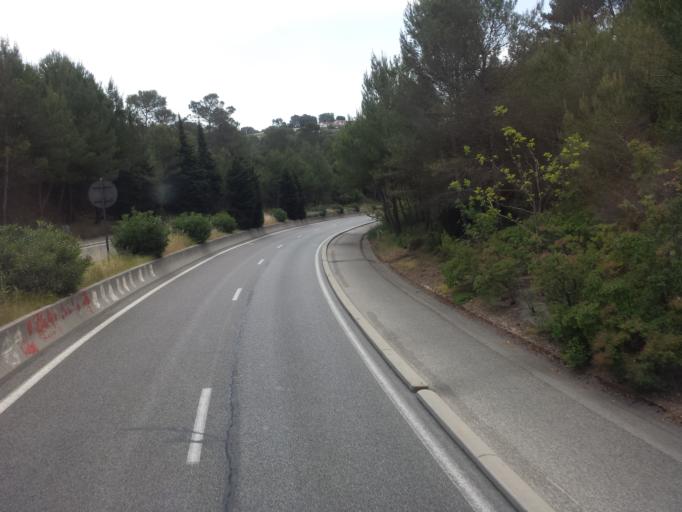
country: FR
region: Provence-Alpes-Cote d'Azur
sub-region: Departement des Alpes-Maritimes
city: Biot
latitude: 43.6110
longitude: 7.0810
